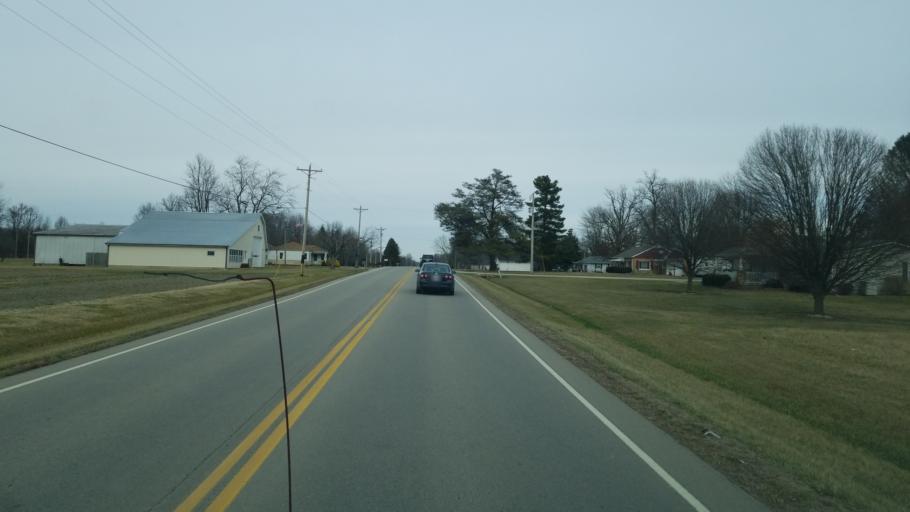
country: US
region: Ohio
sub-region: Adams County
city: Winchester
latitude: 39.0770
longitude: -83.6859
